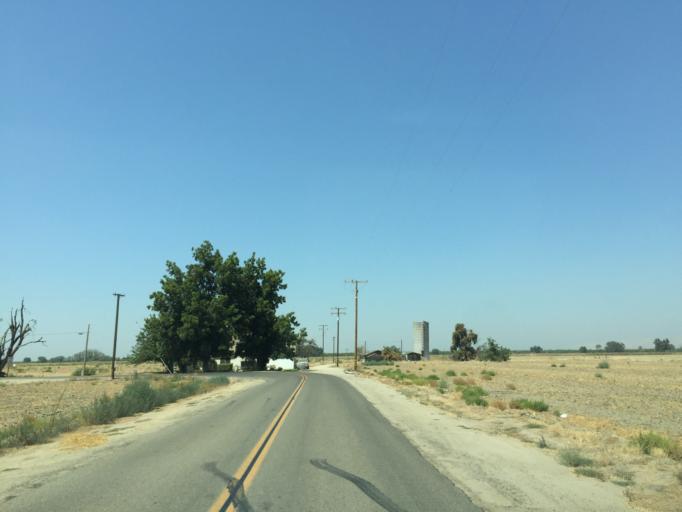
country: US
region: California
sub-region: Tulare County
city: Visalia
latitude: 36.3647
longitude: -119.3144
